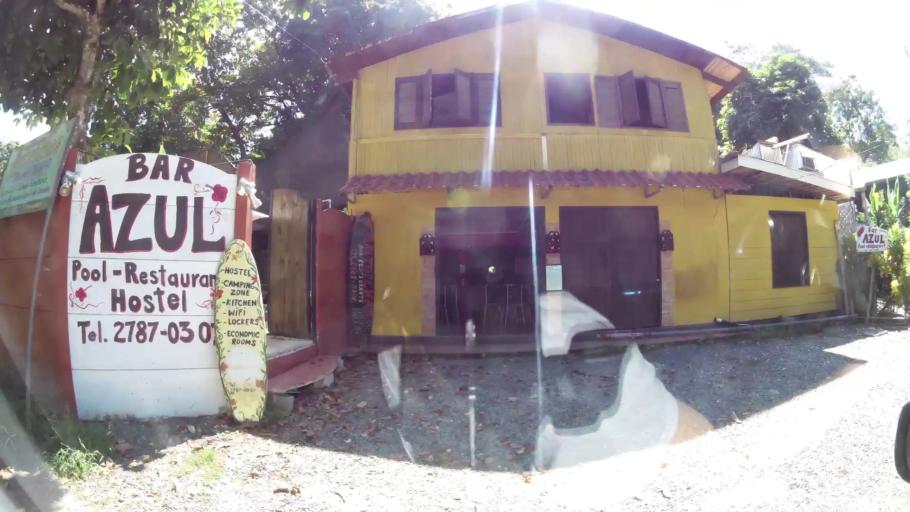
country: CR
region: San Jose
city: San Isidro
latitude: 9.2536
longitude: -83.8658
